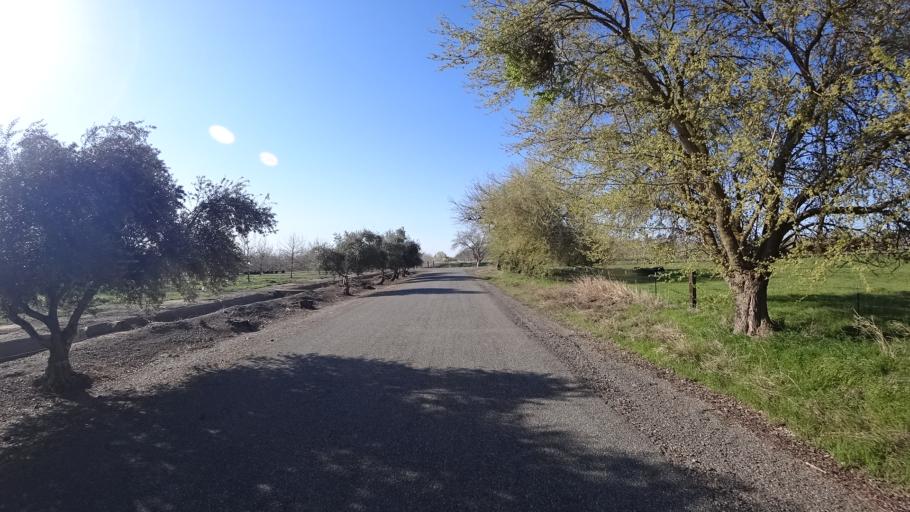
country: US
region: California
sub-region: Glenn County
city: Orland
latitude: 39.7581
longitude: -122.1228
